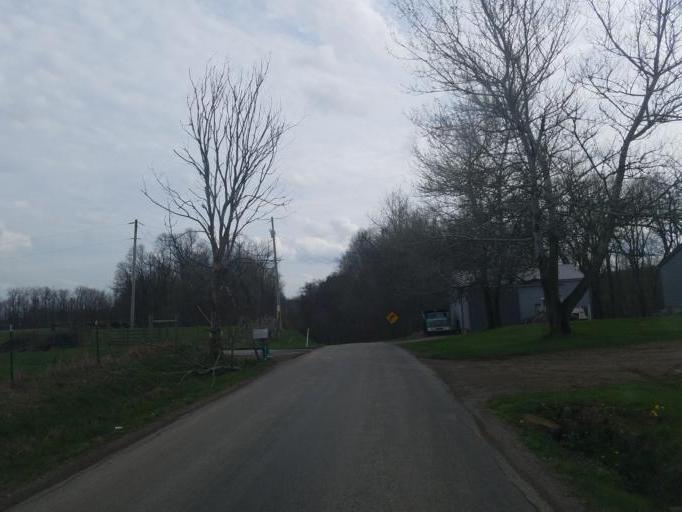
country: US
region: Ohio
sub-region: Richland County
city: Lexington
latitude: 40.5782
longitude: -82.6199
